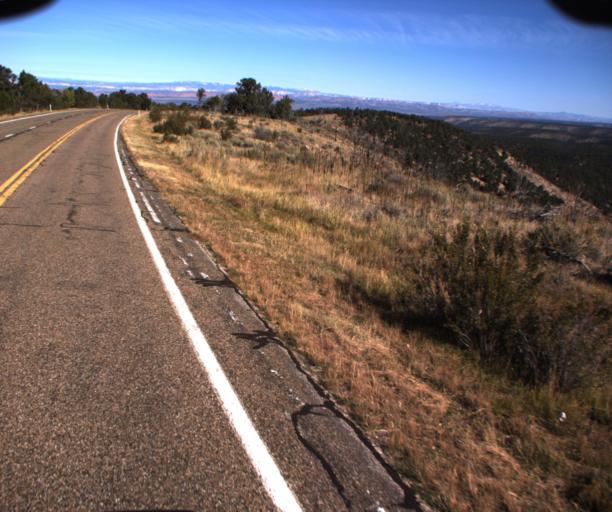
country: US
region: Arizona
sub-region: Coconino County
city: Fredonia
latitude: 36.8054
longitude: -112.2551
